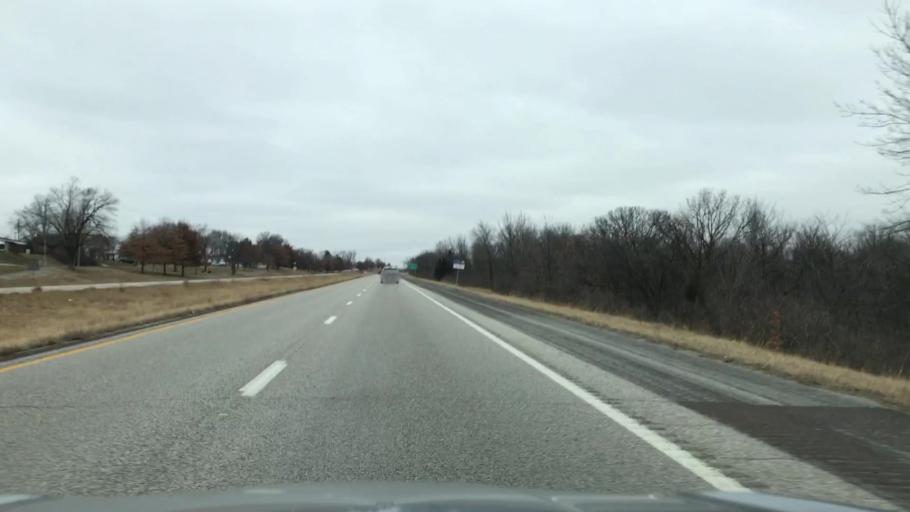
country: US
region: Missouri
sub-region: Clay County
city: Liberty
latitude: 39.2205
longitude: -94.4098
